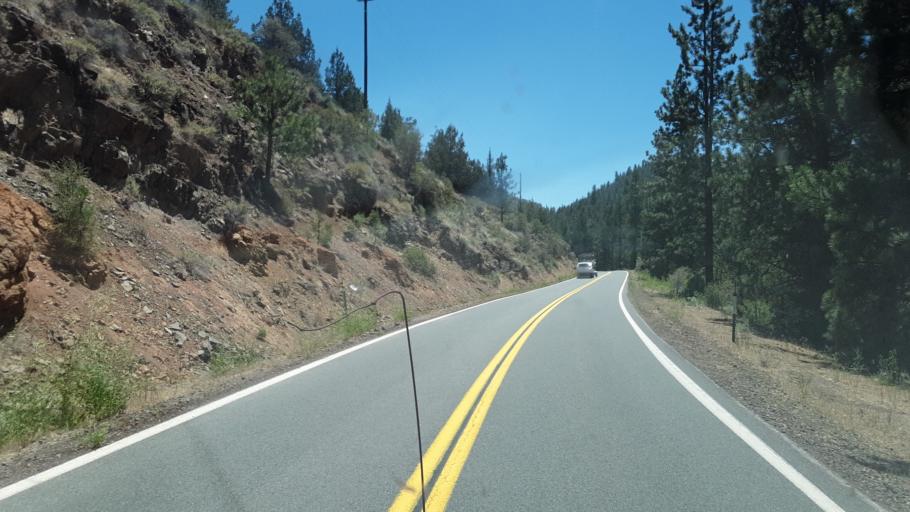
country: US
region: California
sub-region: Modoc County
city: Alturas
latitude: 41.0297
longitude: -120.8544
